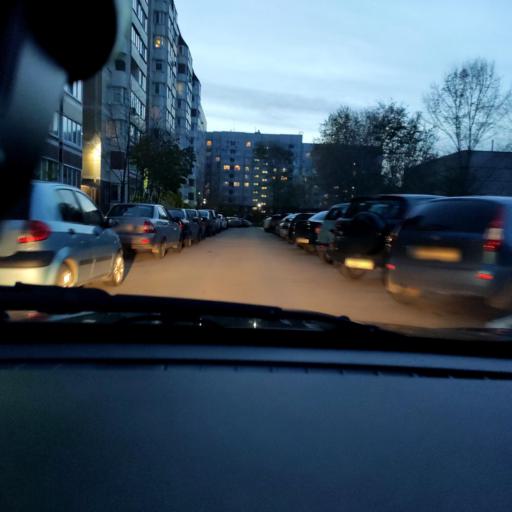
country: RU
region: Samara
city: Tol'yatti
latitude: 53.5313
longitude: 49.3929
